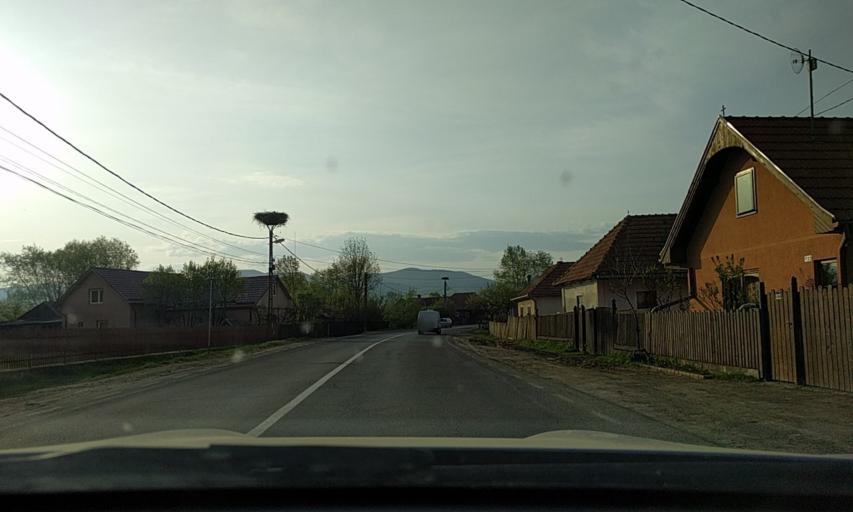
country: RO
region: Covasna
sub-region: Comuna Lemnia
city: Lemnia
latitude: 46.0461
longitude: 26.2675
